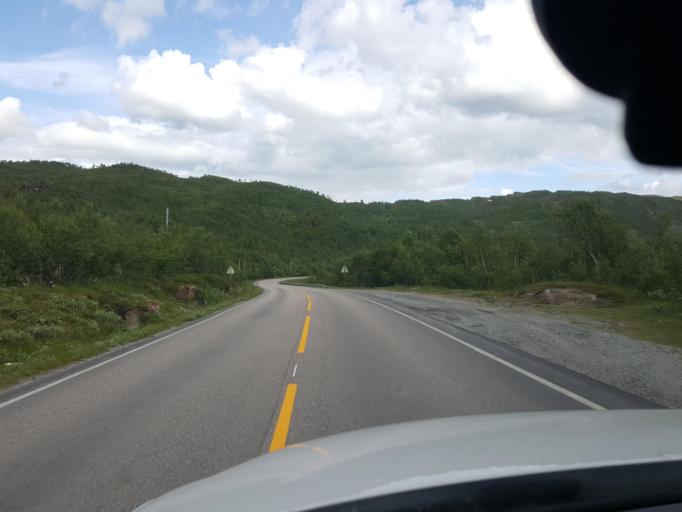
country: NO
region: Nordland
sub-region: Rana
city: Mo i Rana
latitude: 66.2891
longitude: 14.4909
